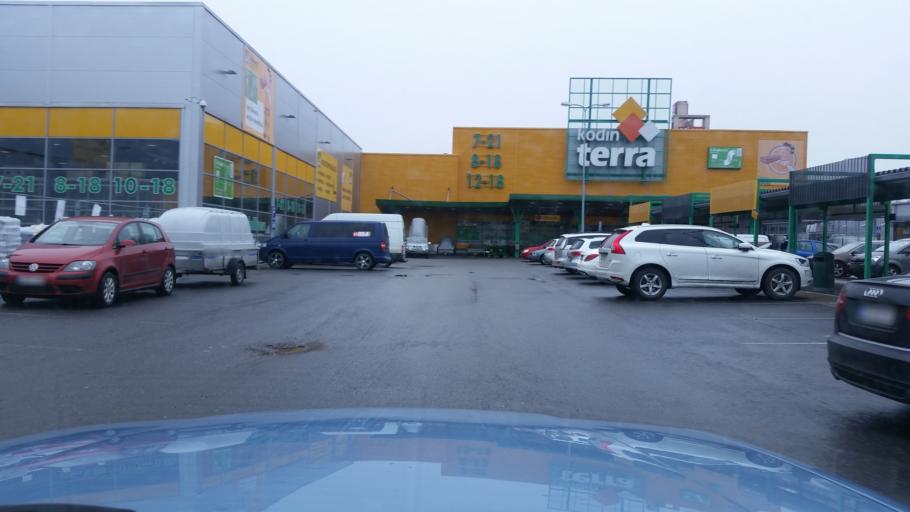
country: FI
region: Haeme
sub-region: Haemeenlinna
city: Haemeenlinna
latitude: 61.0088
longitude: 24.4186
